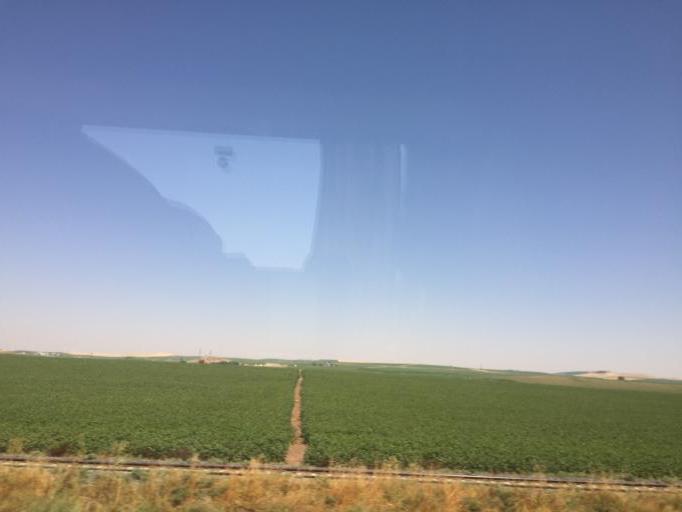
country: TR
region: Diyarbakir
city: Tepe
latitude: 37.8510
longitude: 40.7599
